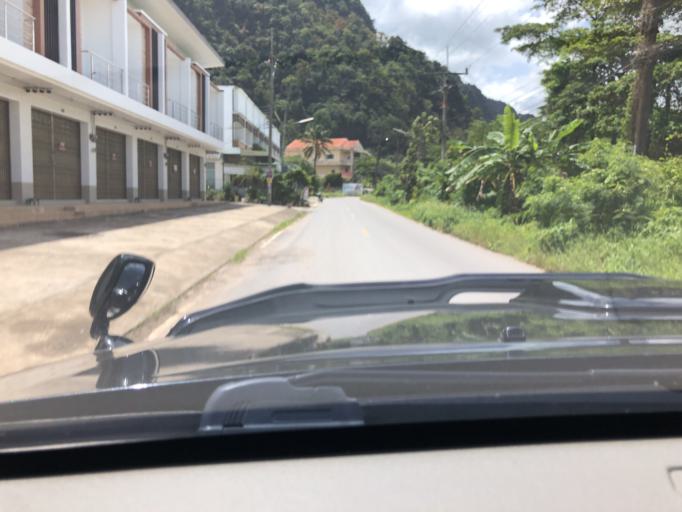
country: TH
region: Krabi
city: Krabi
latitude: 8.1198
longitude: 98.9241
